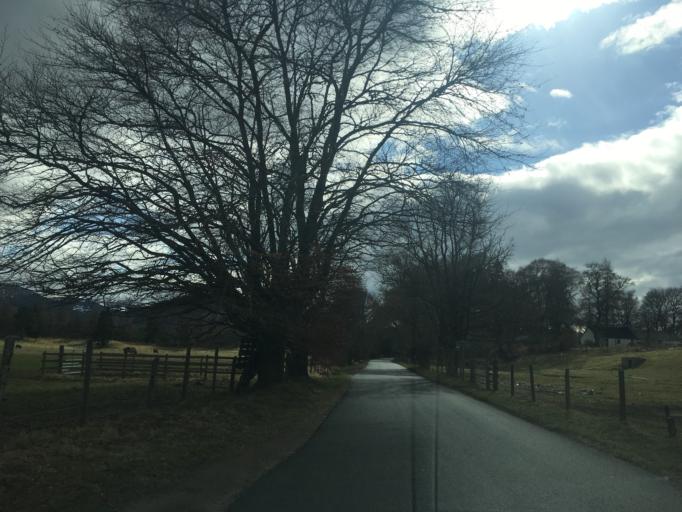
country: GB
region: Scotland
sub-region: Highland
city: Aviemore
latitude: 57.1751
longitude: -3.8202
